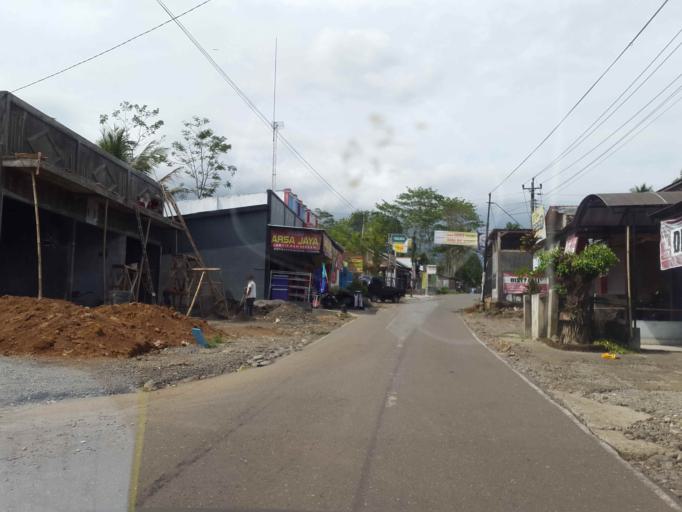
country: ID
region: Central Java
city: Purwokerto
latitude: -7.3672
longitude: 109.2748
